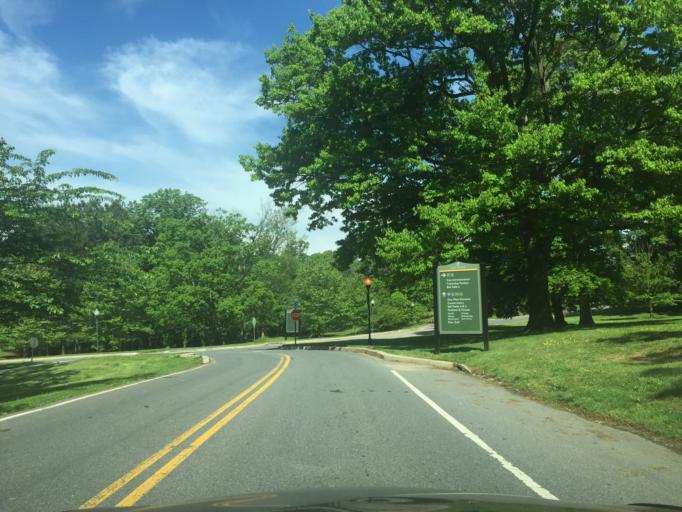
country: US
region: Maryland
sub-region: City of Baltimore
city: Baltimore
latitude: 39.3197
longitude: -76.6416
